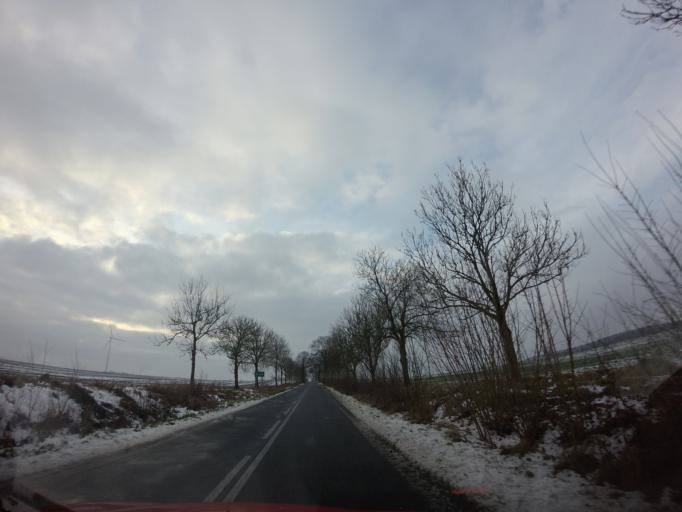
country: PL
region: West Pomeranian Voivodeship
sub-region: Powiat choszczenski
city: Krzecin
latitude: 53.0775
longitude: 15.4591
